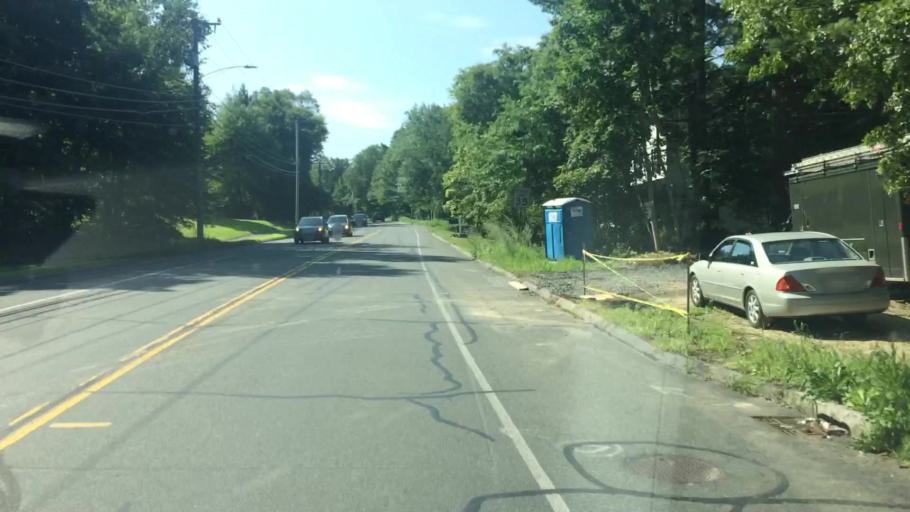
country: US
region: Massachusetts
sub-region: Hampshire County
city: South Amherst
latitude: 42.3538
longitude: -72.5206
